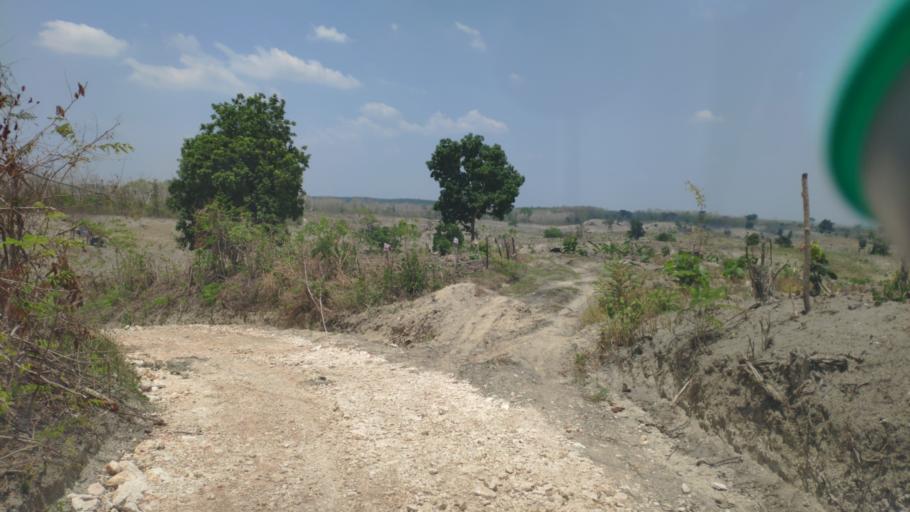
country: ID
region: Central Java
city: Randublatung
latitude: -7.2752
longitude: 111.3318
